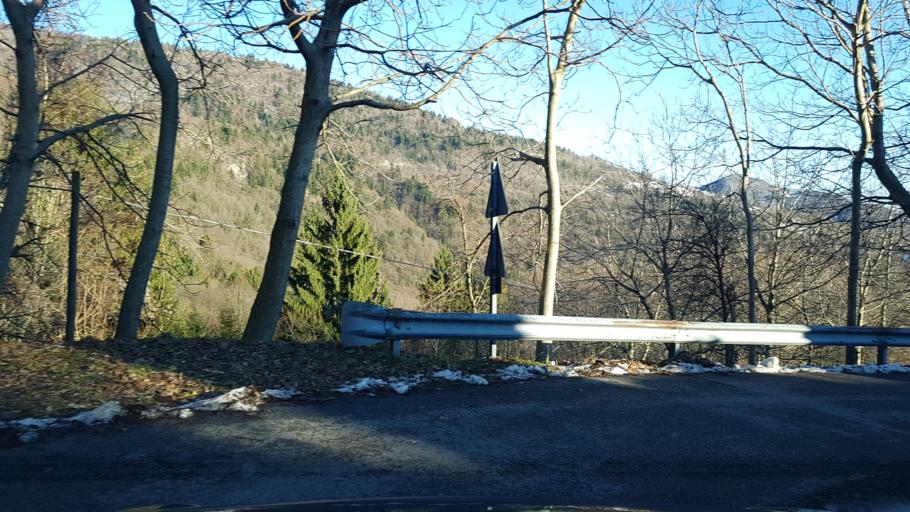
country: IT
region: Friuli Venezia Giulia
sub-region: Provincia di Udine
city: Savogna
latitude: 46.1871
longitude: 13.5335
